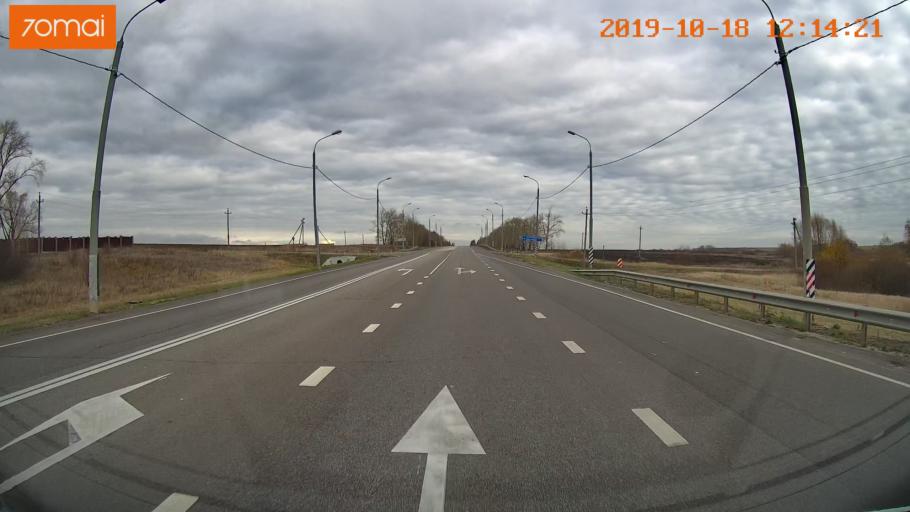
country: RU
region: Rjazan
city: Zakharovo
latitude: 54.4297
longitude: 39.3818
